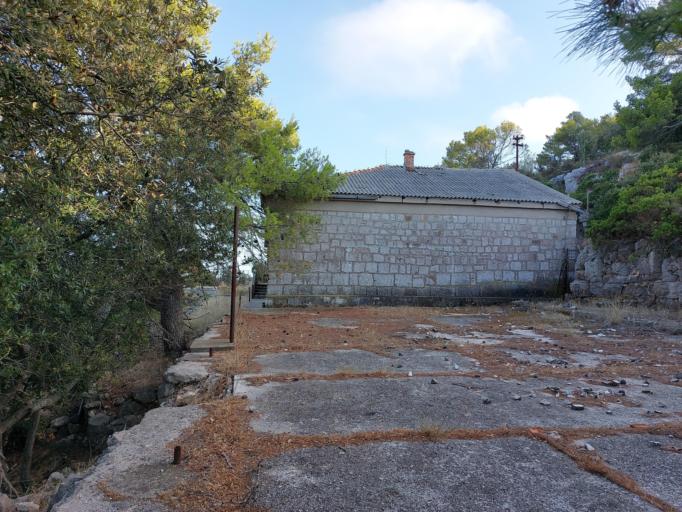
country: HR
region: Dubrovacko-Neretvanska
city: Smokvica
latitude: 42.7525
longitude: 16.8620
